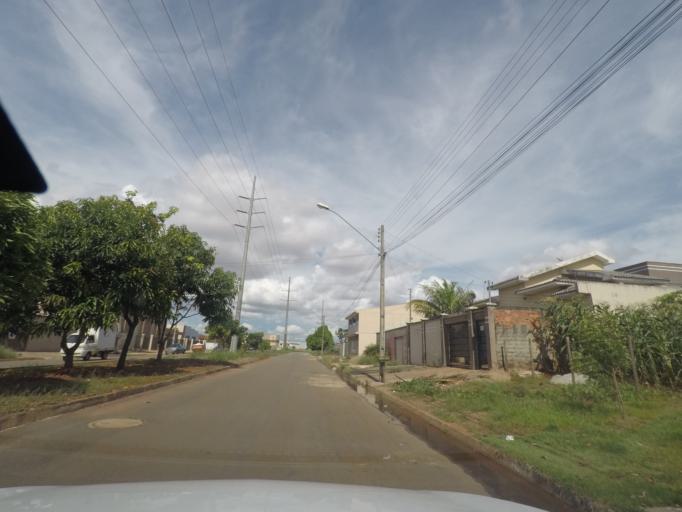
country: BR
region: Goias
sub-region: Goiania
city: Goiania
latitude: -16.7212
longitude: -49.3486
